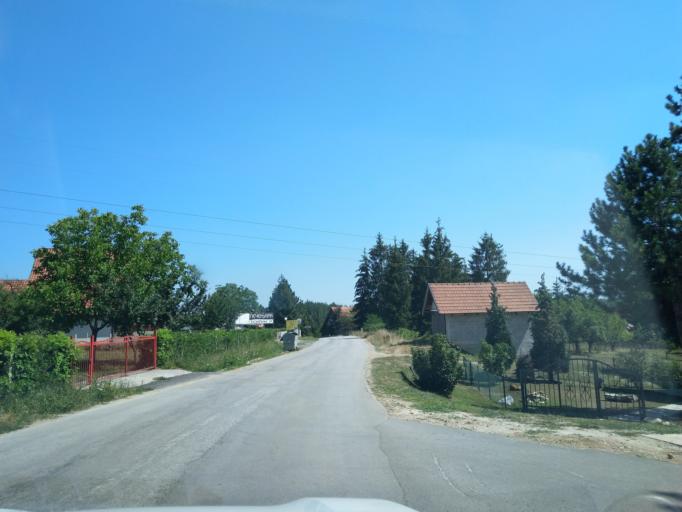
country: RS
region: Central Serbia
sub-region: Zlatiborski Okrug
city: Uzice
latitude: 43.8064
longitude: 19.8114
